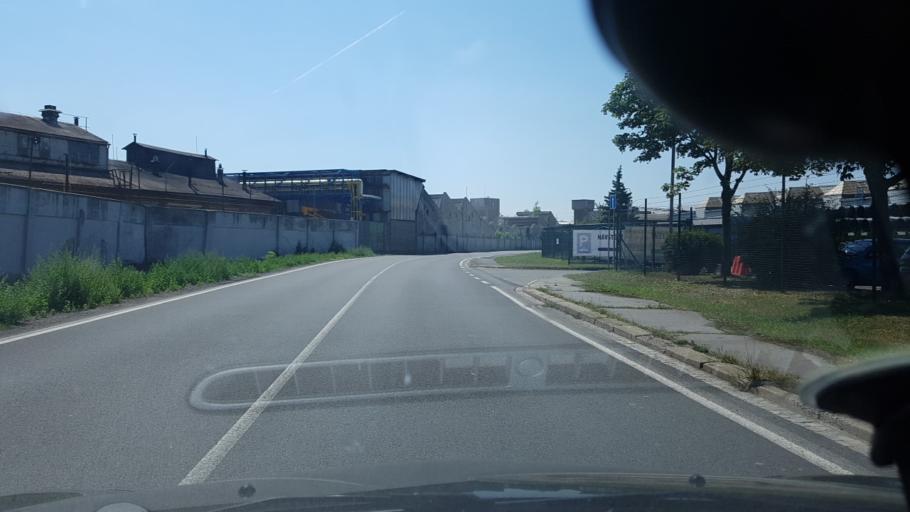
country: CZ
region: Moravskoslezsky
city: Bohumin
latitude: 49.8957
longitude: 18.3435
